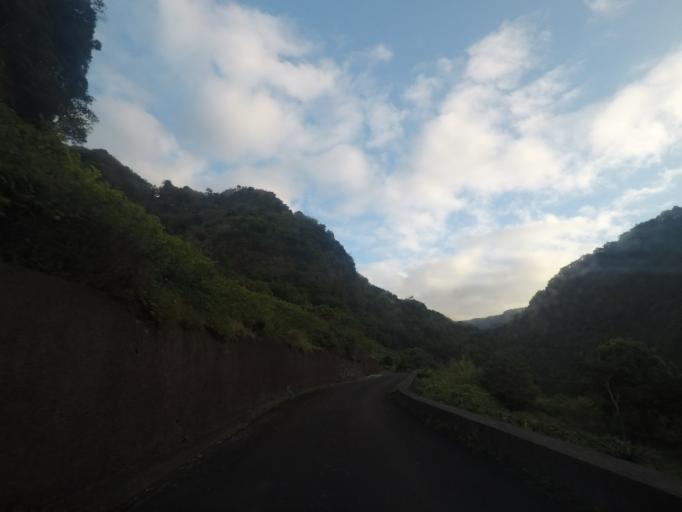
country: PT
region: Madeira
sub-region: Porto Moniz
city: Porto Moniz
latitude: 32.8488
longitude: -17.1611
